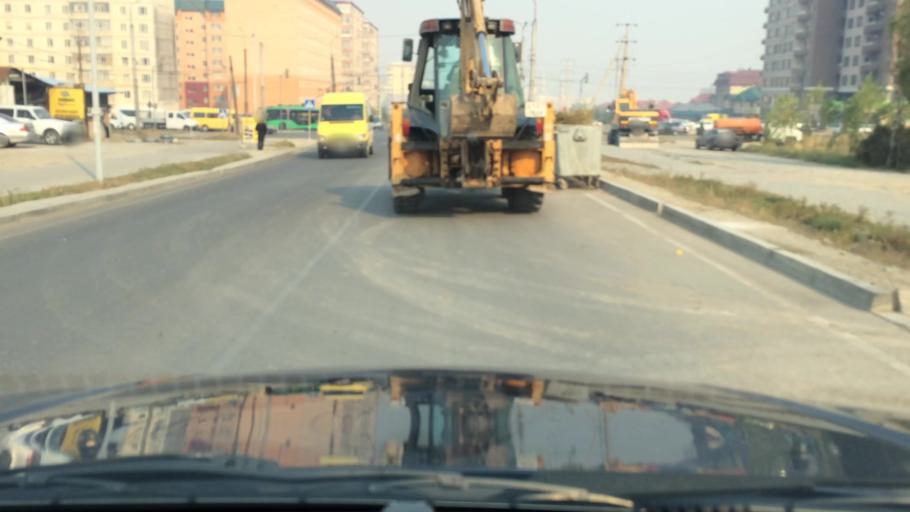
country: KG
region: Chuy
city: Bishkek
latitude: 42.8286
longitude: 74.5695
